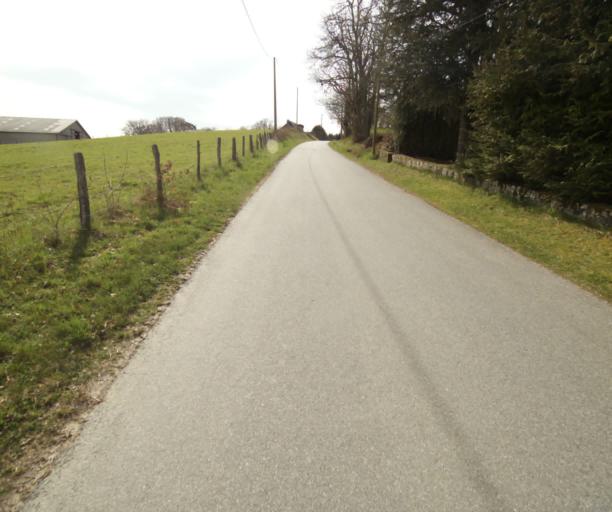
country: FR
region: Limousin
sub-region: Departement de la Correze
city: Correze
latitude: 45.3693
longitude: 1.8837
